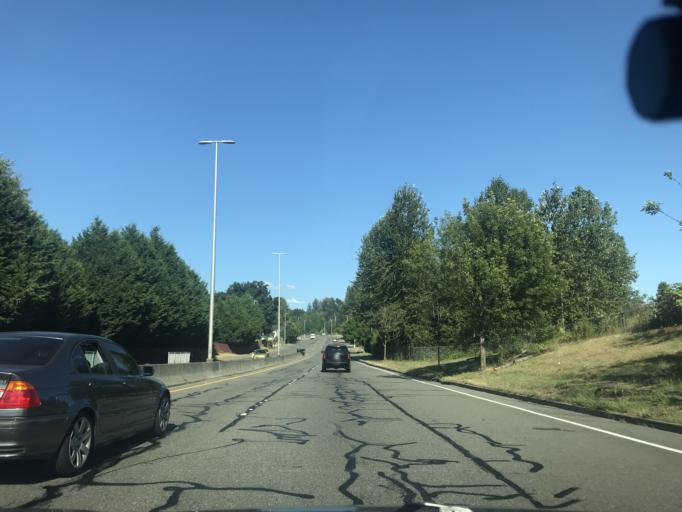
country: US
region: Washington
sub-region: King County
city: Lea Hill
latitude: 47.3559
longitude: -122.1955
